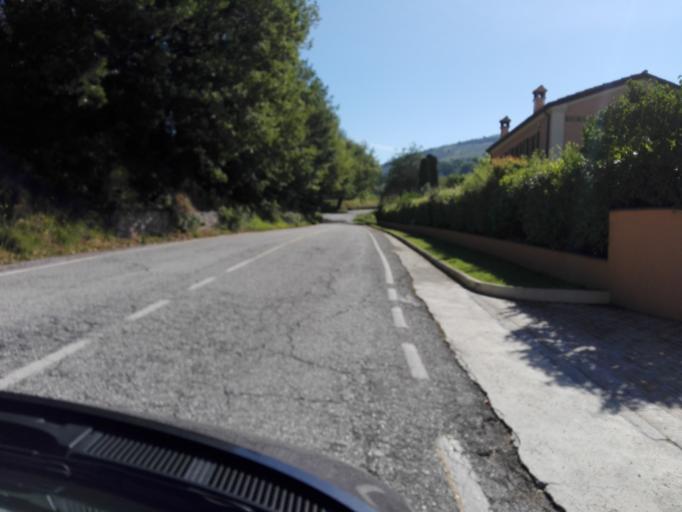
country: IT
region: Umbria
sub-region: Provincia di Perugia
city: Foligno
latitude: 42.9663
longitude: 12.7400
